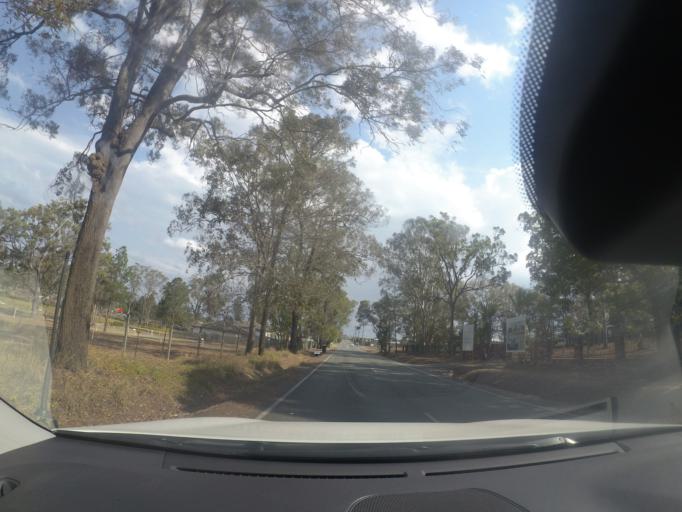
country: AU
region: Queensland
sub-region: Logan
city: Rochedale South
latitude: -27.5917
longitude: 153.1061
